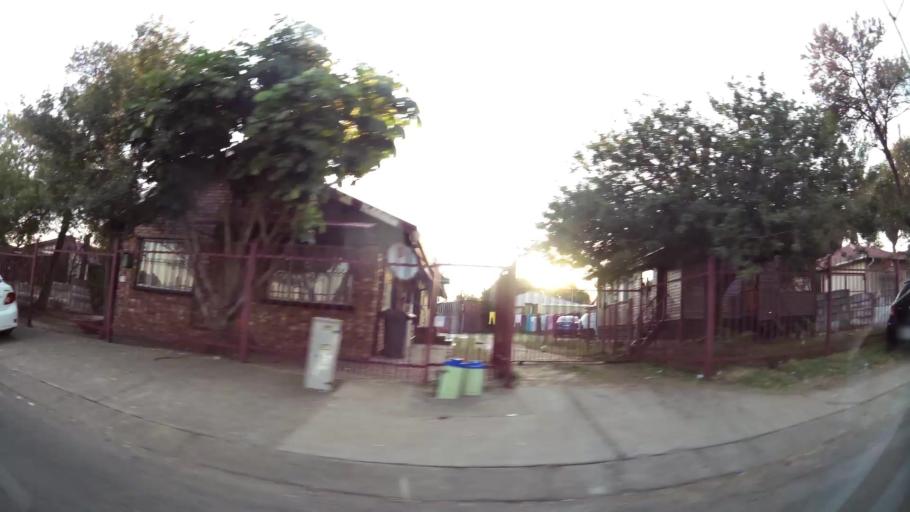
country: ZA
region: Gauteng
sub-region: City of Tshwane Metropolitan Municipality
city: Pretoria
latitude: -25.7416
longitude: 28.1349
